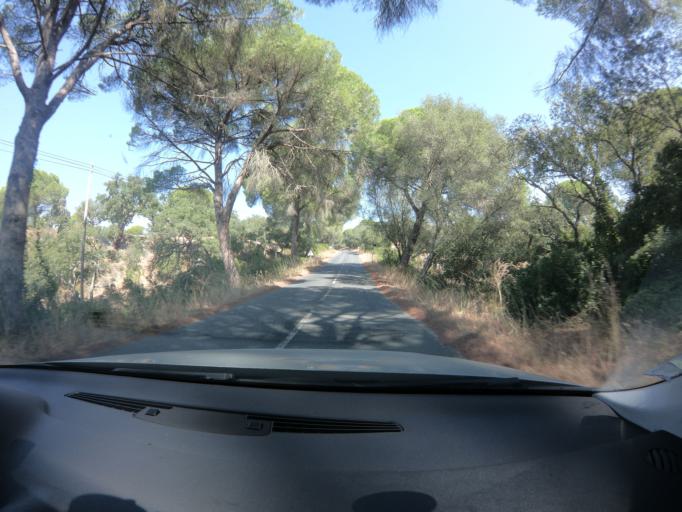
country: PT
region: Setubal
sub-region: Alcacer do Sal
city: Alcacer do Sal
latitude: 38.2962
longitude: -8.4050
